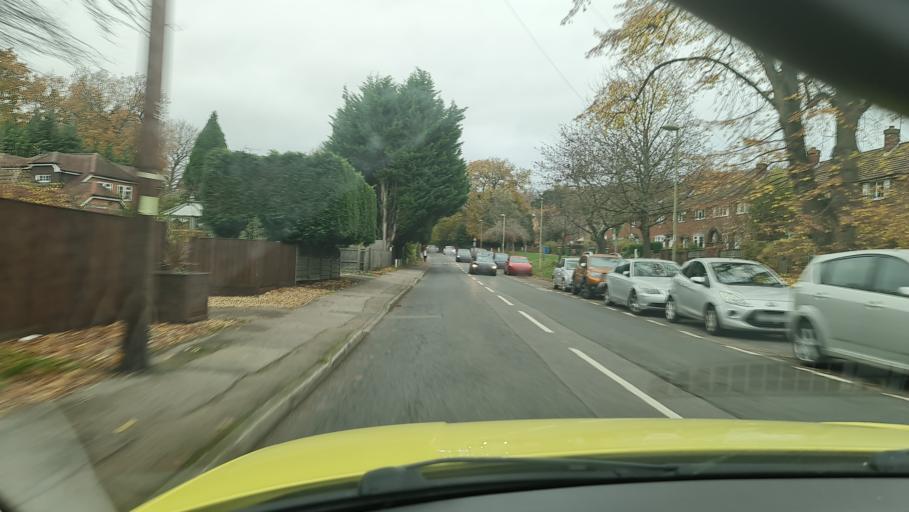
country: GB
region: England
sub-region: Hampshire
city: Farnborough
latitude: 51.3145
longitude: -0.7766
